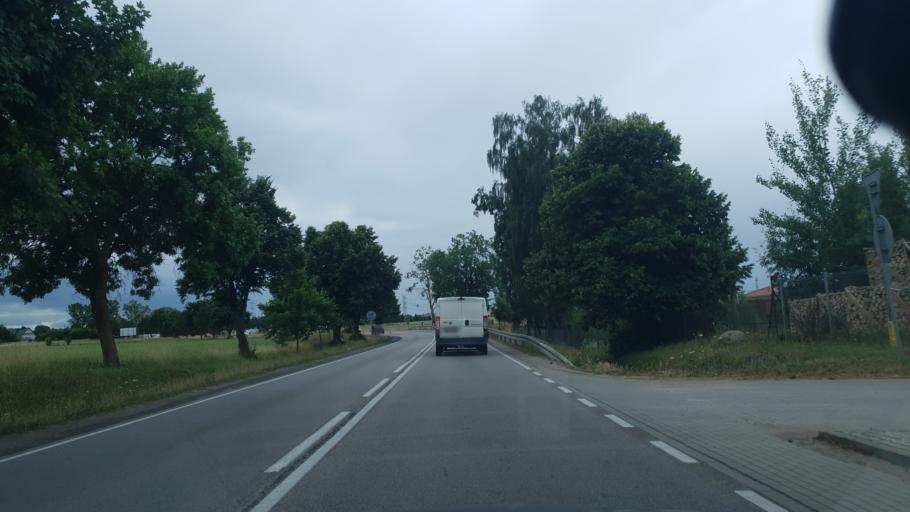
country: PL
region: Pomeranian Voivodeship
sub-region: Powiat kartuski
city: Banino
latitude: 54.3948
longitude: 18.3570
